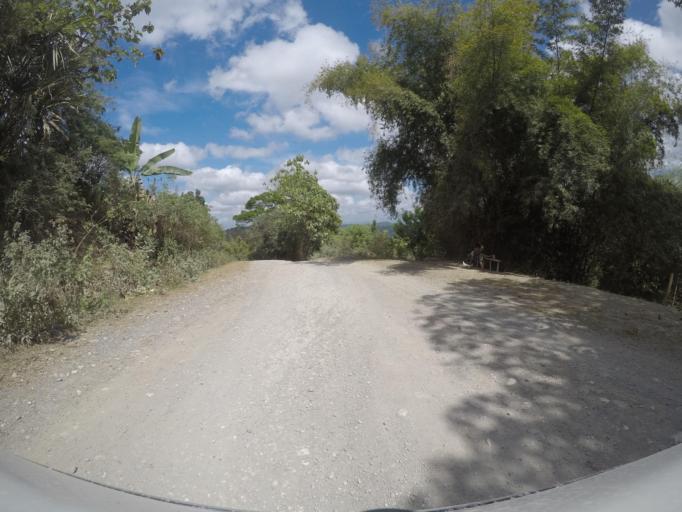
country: TL
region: Viqueque
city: Viqueque
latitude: -8.8682
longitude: 126.3301
